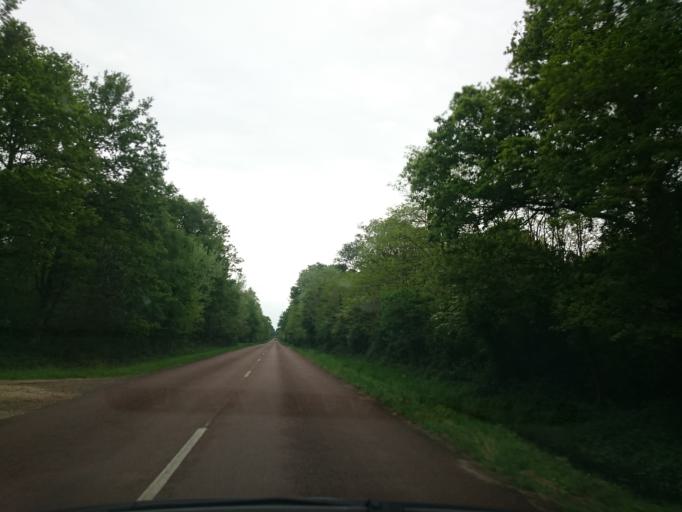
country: FR
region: Centre
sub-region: Departement du Loir-et-Cher
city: Muides-sur-Loire
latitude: 47.6484
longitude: 1.5280
